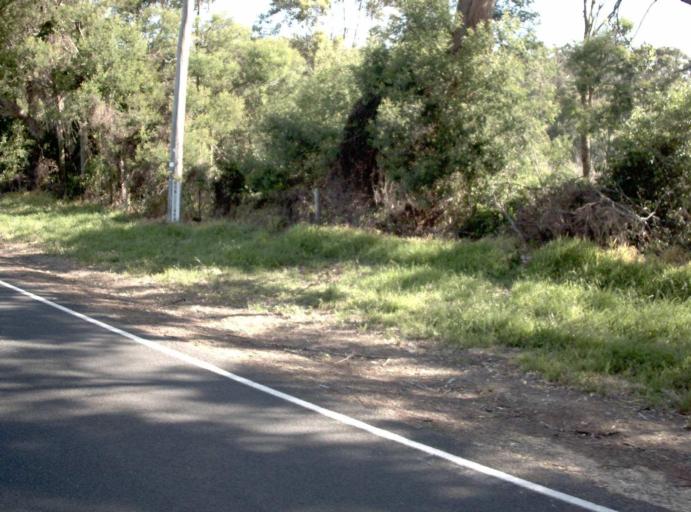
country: AU
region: Victoria
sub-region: East Gippsland
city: Lakes Entrance
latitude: -37.7505
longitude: 148.5192
